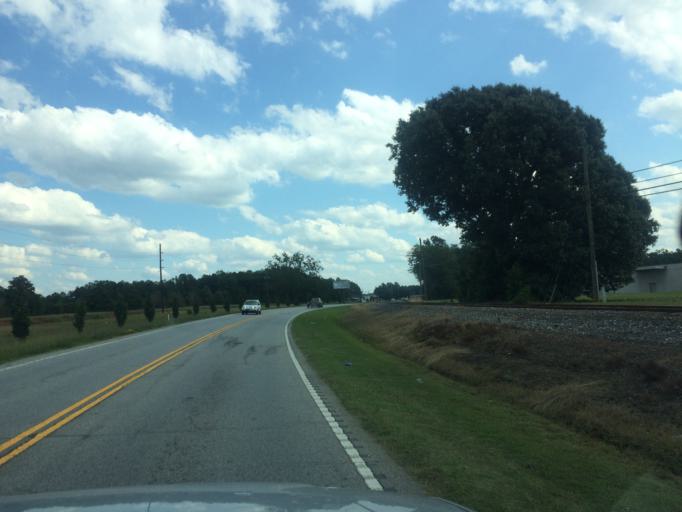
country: US
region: South Carolina
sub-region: Anderson County
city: Belton
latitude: 34.5137
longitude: -82.4785
